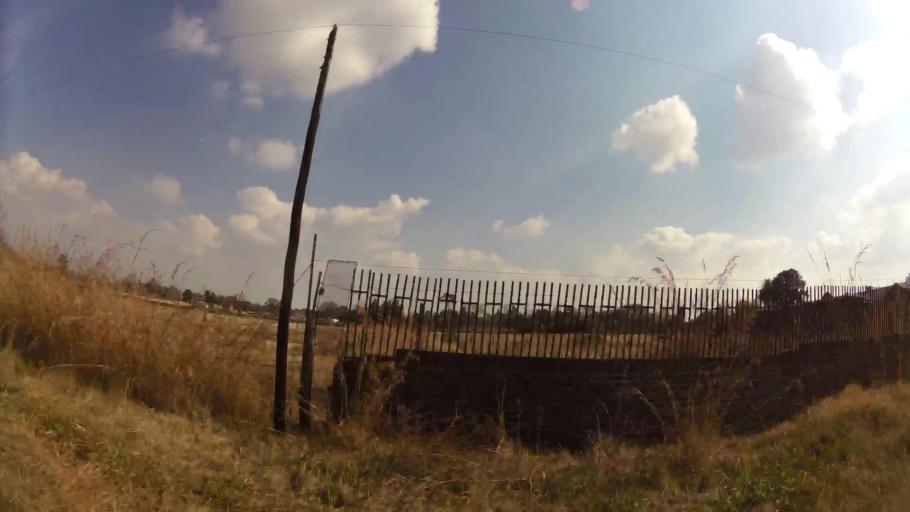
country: ZA
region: Mpumalanga
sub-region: Nkangala District Municipality
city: Delmas
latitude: -26.1782
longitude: 28.5406
